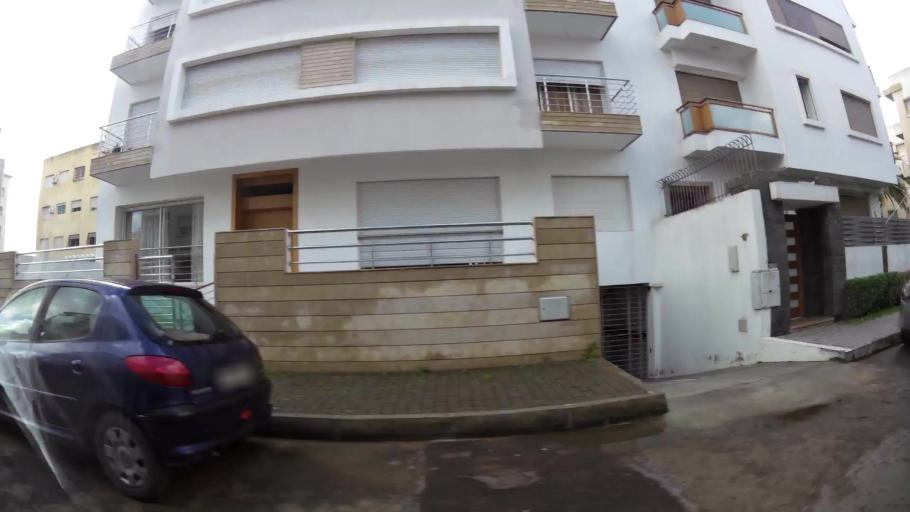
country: MA
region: Grand Casablanca
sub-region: Casablanca
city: Casablanca
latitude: 33.5539
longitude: -7.6272
